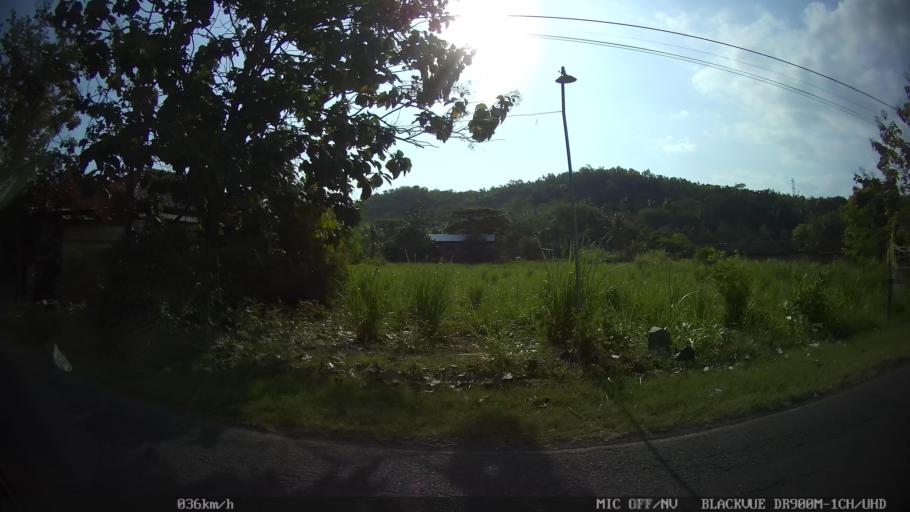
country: ID
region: Daerah Istimewa Yogyakarta
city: Bantul
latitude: -7.8837
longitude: 110.3052
